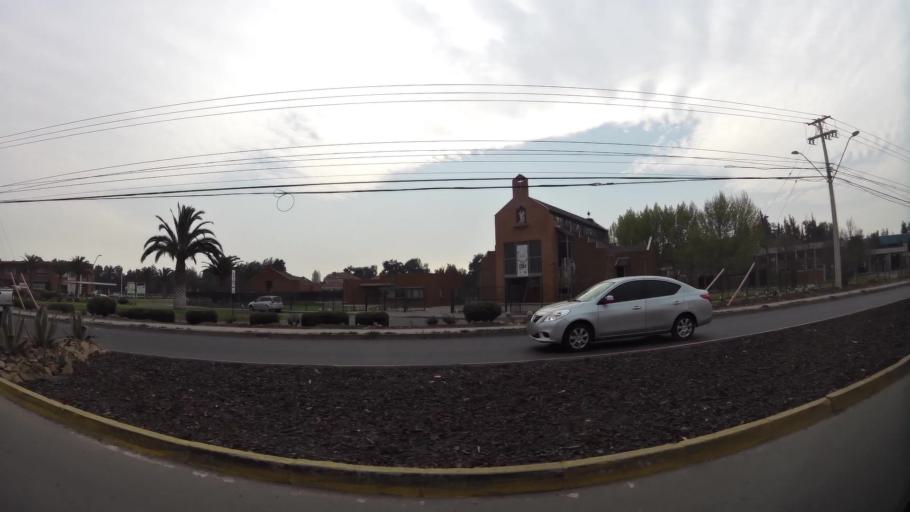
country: CL
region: Santiago Metropolitan
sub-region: Provincia de Chacabuco
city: Chicureo Abajo
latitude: -33.2763
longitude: -70.7025
